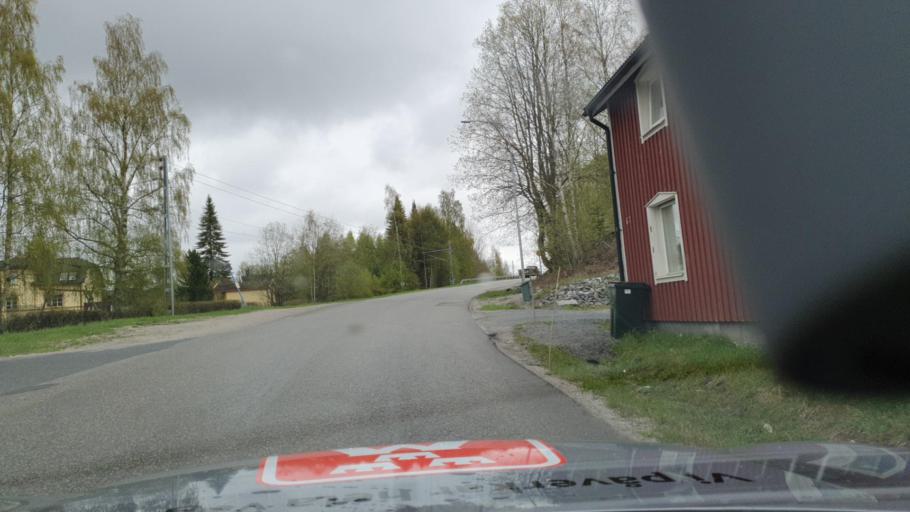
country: SE
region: Vaesternorrland
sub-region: OErnskoeldsviks Kommun
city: Ornskoldsvik
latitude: 63.2972
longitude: 18.5980
